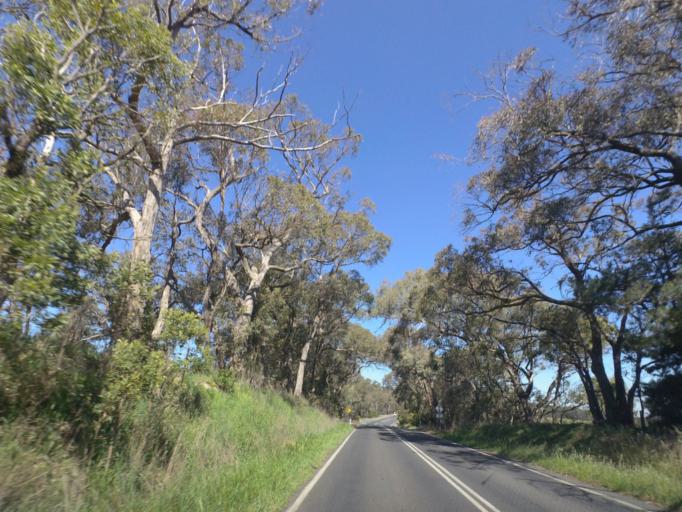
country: AU
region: Victoria
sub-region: Whittlesea
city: Whittlesea
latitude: -37.3443
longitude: 144.9966
